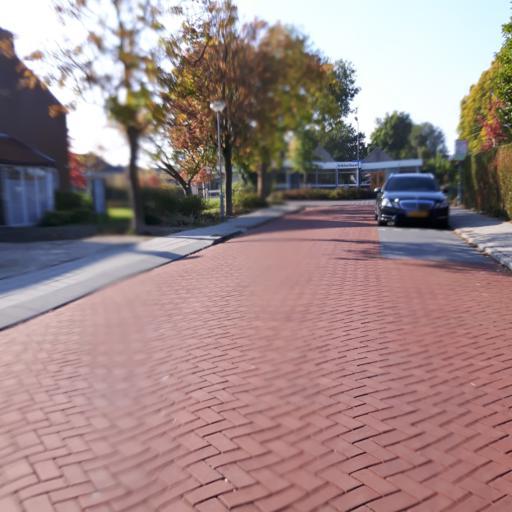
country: NL
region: Zeeland
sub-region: Gemeente Goes
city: Goes
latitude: 51.4837
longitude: 3.9579
